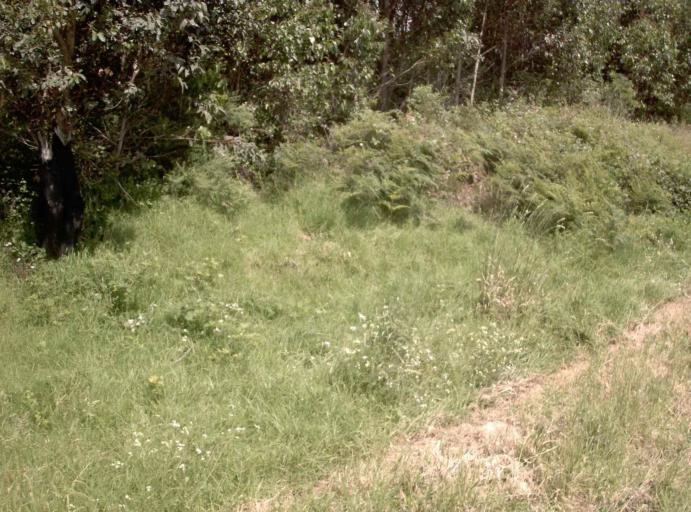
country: AU
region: Victoria
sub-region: Latrobe
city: Traralgon
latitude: -38.3355
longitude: 146.5723
